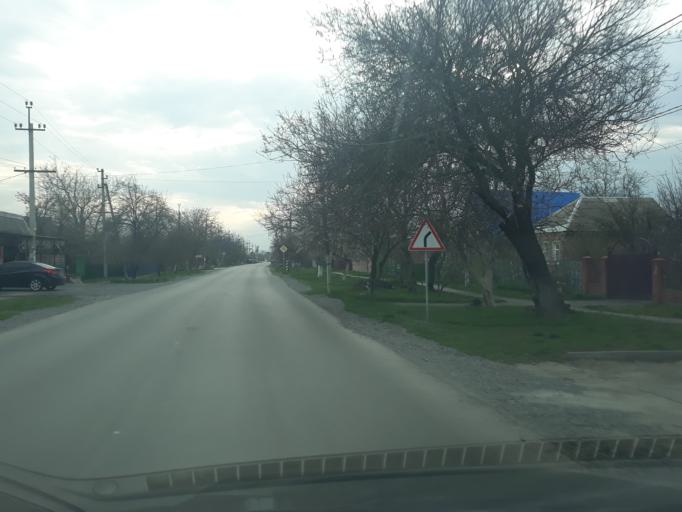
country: RU
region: Rostov
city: Novobessergenovka
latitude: 47.1615
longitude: 38.7214
